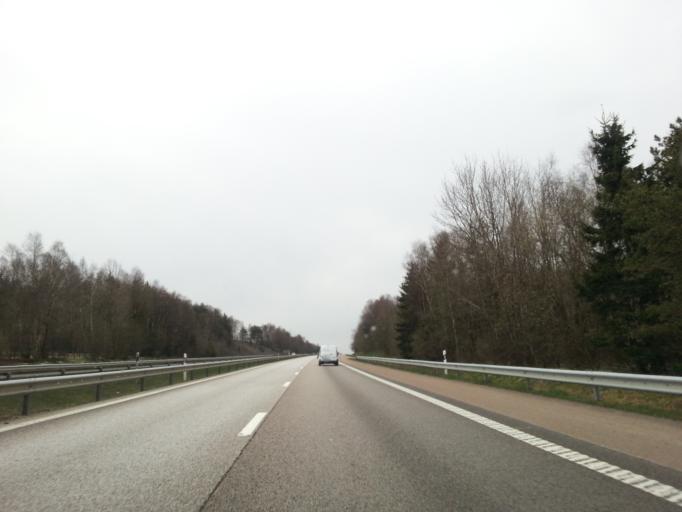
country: SE
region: Skane
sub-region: Bastads Kommun
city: Bastad
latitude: 56.3940
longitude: 12.9409
